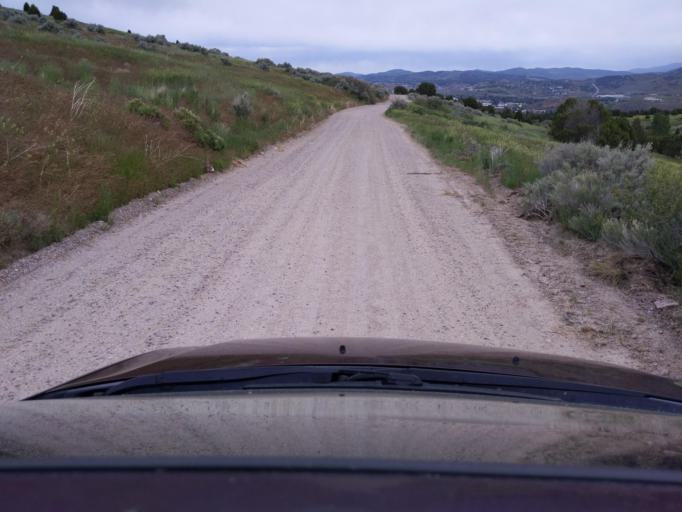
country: US
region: Idaho
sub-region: Bannock County
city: Pocatello
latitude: 42.8421
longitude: -112.4611
